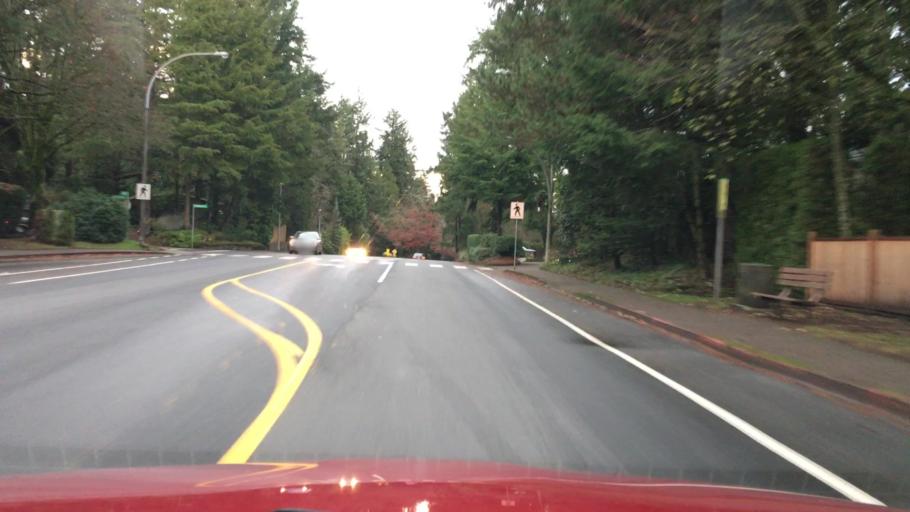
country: CA
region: British Columbia
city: Victoria
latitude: 48.4998
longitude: -123.3670
